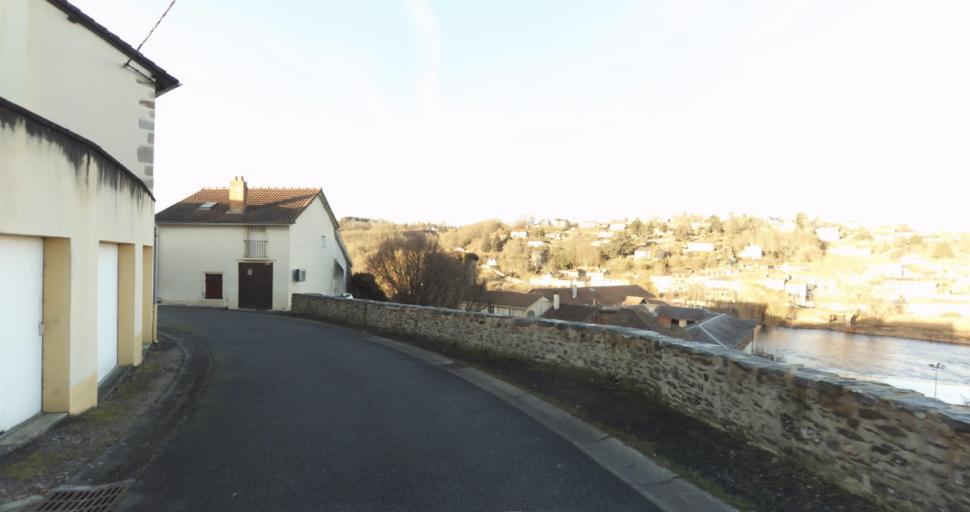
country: FR
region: Limousin
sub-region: Departement de la Haute-Vienne
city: Aixe-sur-Vienne
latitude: 45.7956
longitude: 1.1427
